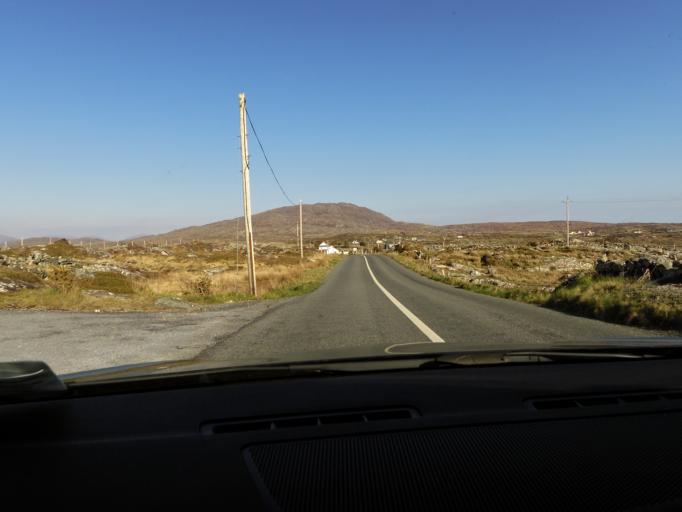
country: IE
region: Connaught
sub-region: County Galway
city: Clifden
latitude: 53.3951
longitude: -10.0135
